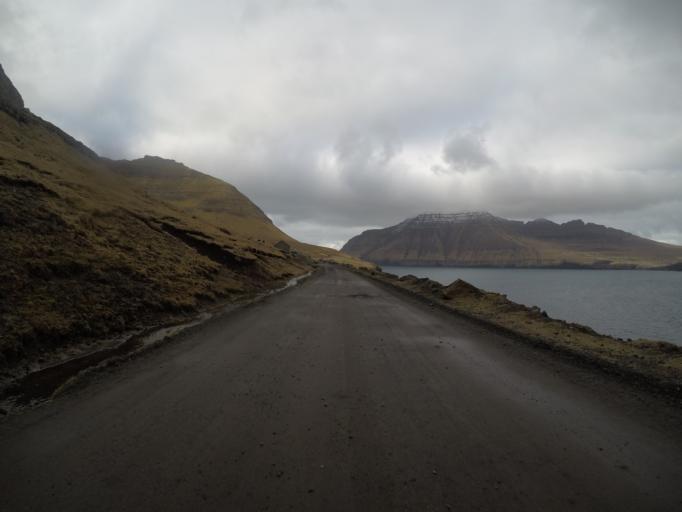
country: FO
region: Nordoyar
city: Klaksvik
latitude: 62.3456
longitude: -6.5802
